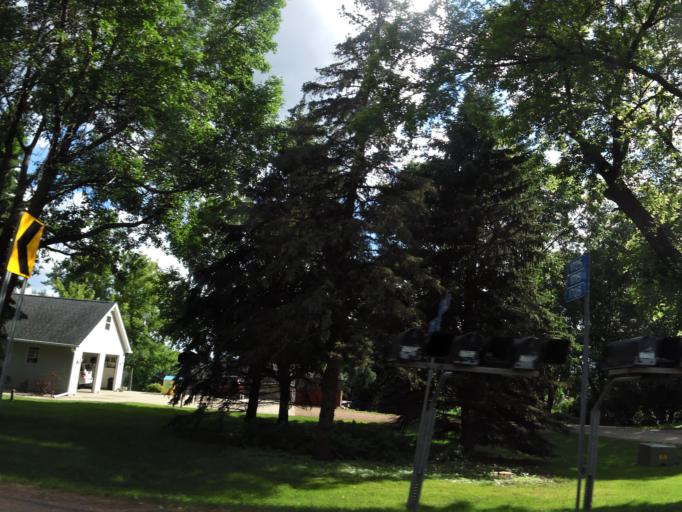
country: US
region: Minnesota
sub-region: Carver County
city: Waconia
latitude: 44.8412
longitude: -93.8181
